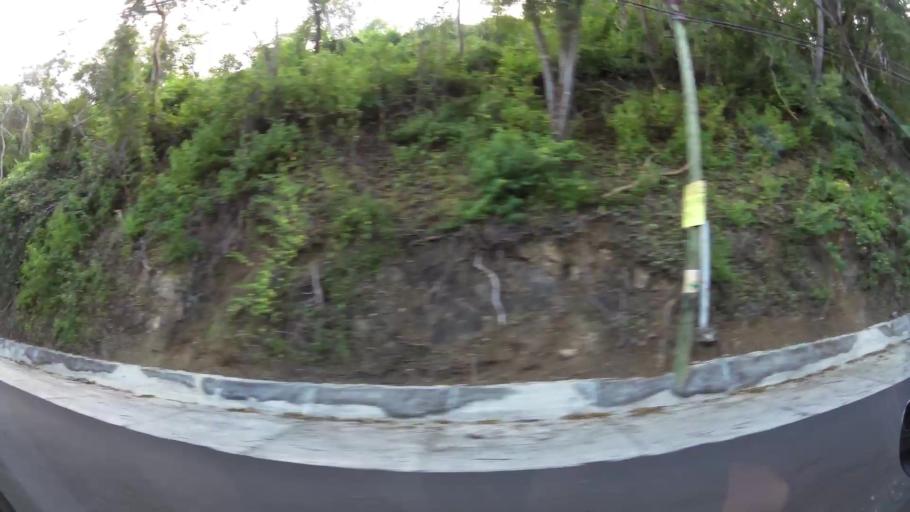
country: CR
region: Guanacaste
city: Sardinal
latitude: 10.5654
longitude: -85.6796
